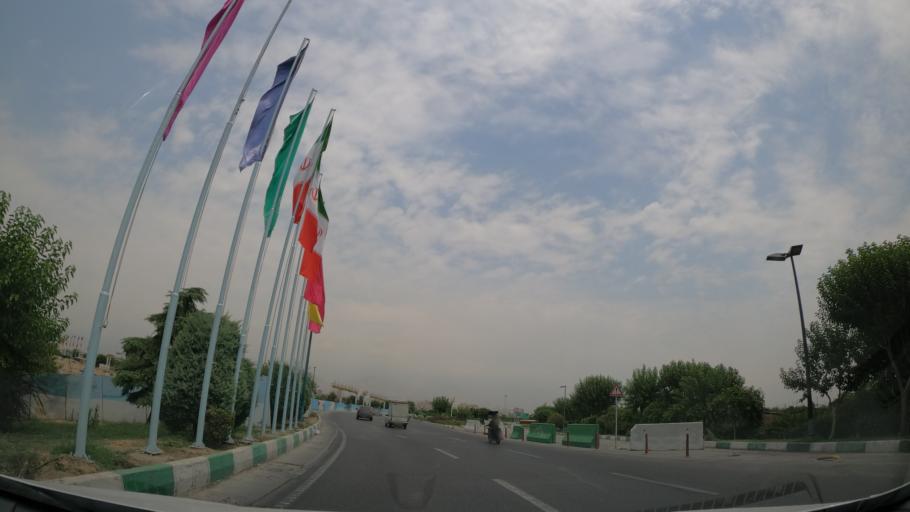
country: IR
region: Tehran
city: Tehran
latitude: 35.6791
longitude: 51.3413
